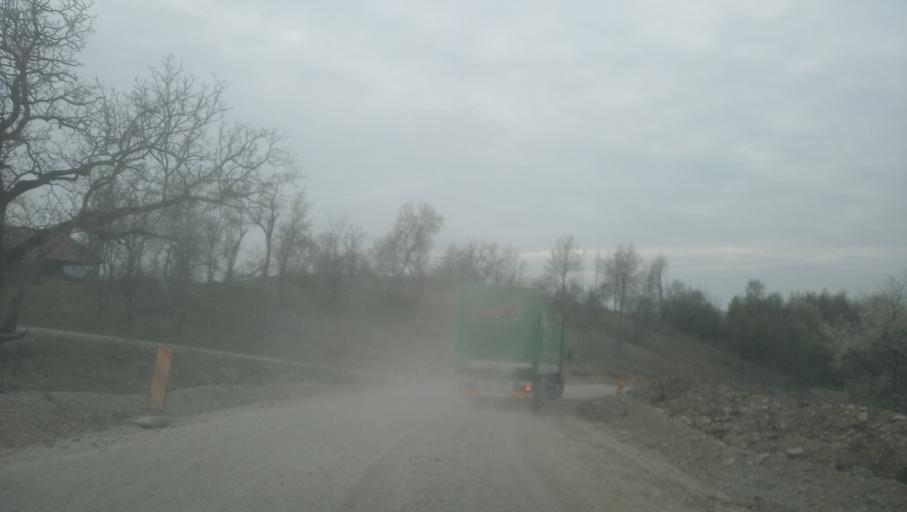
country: RO
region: Arad
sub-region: Comuna Varfurile
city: Varfurile
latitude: 46.3478
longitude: 22.5532
